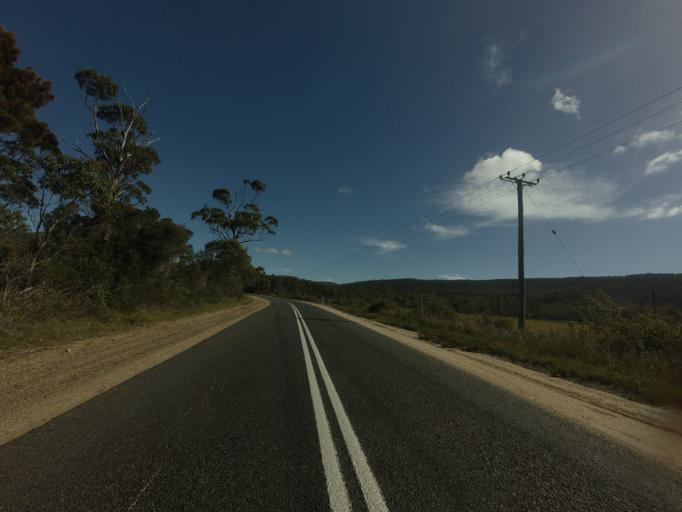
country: AU
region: Tasmania
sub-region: Break O'Day
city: St Helens
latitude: -41.8342
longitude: 148.2553
